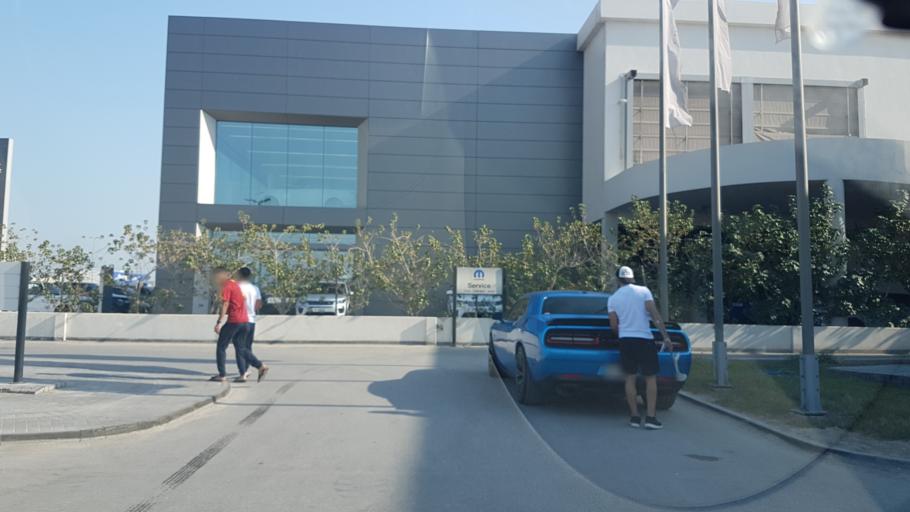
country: BH
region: Northern
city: Sitrah
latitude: 26.1549
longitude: 50.6097
